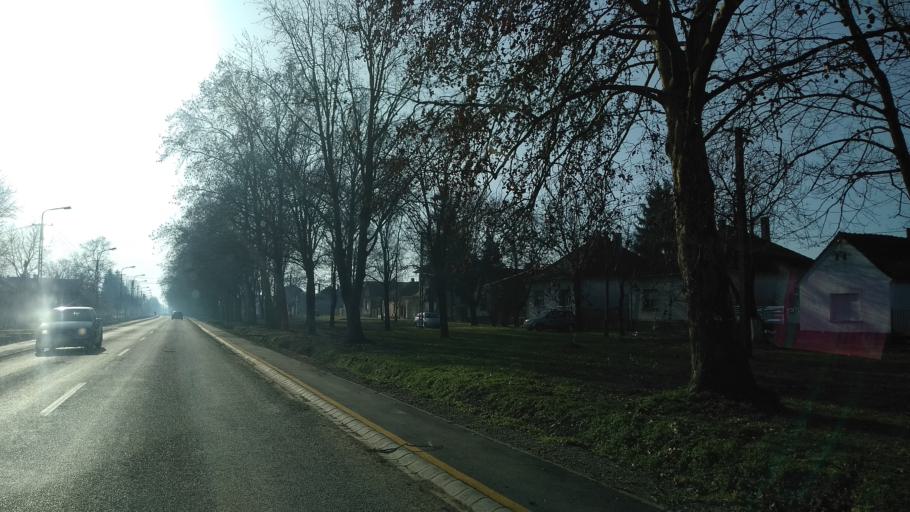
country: HU
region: Somogy
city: Barcs
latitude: 45.9712
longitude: 17.4587
